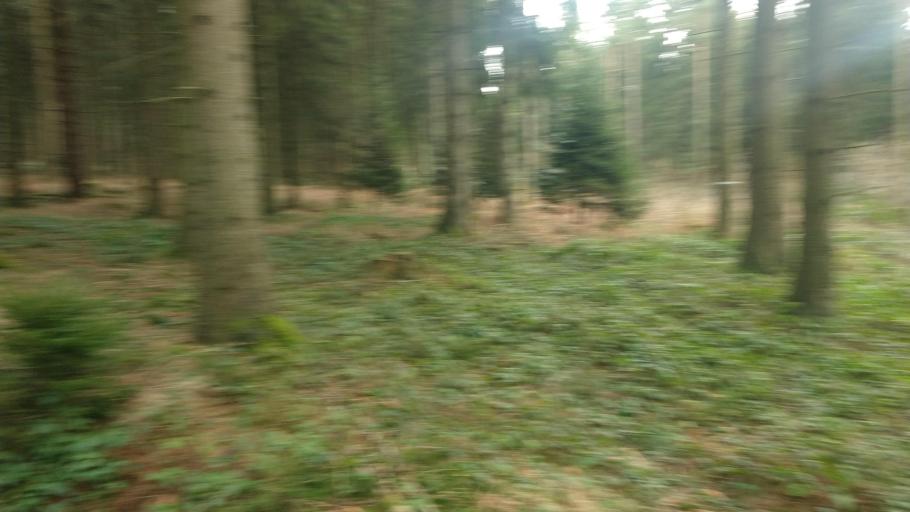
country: DE
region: Lower Saxony
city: Nienstadt
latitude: 52.2620
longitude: 9.1709
